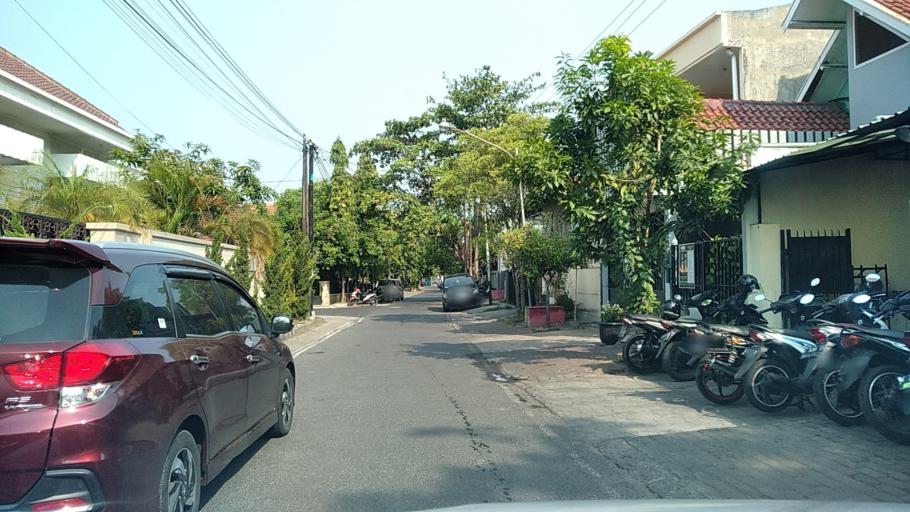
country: ID
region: Central Java
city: Semarang
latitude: -6.9984
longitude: 110.4262
